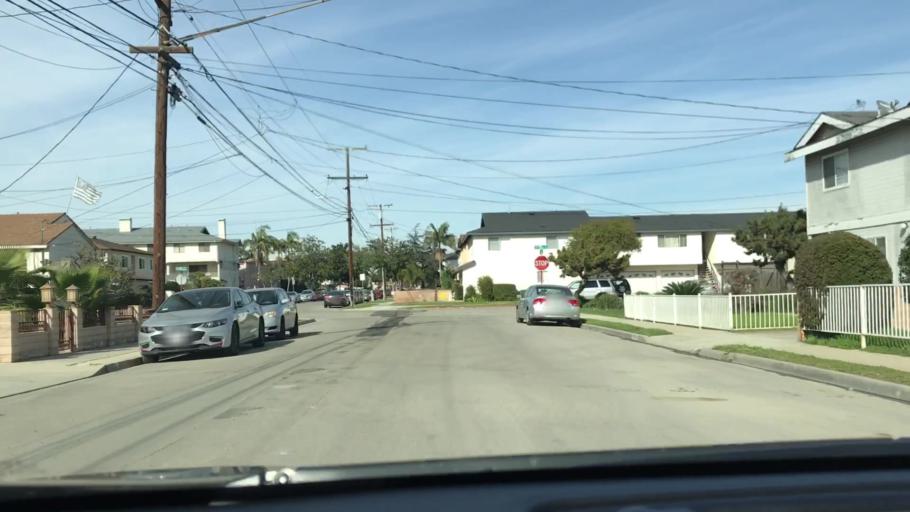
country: US
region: California
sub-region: Los Angeles County
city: Gardena
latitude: 33.8760
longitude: -118.3037
